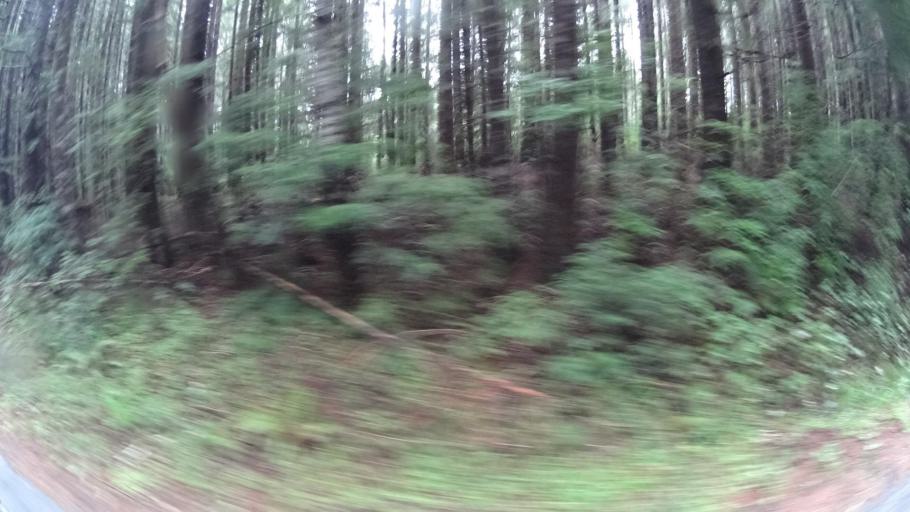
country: US
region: California
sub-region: Humboldt County
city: Westhaven-Moonstone
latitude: 41.2364
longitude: -123.9806
